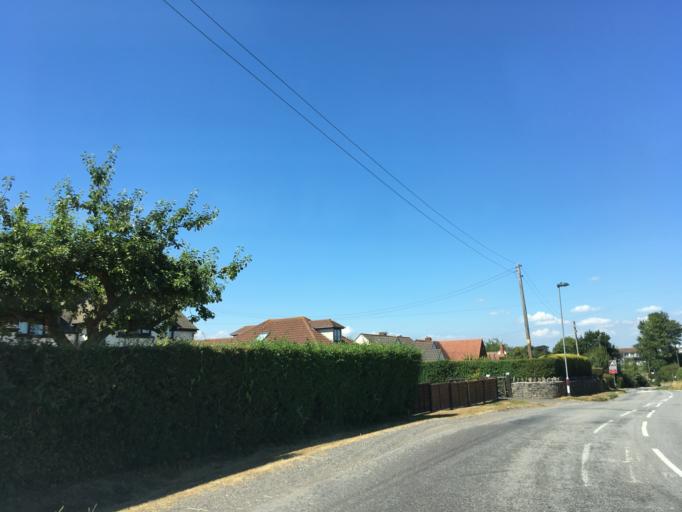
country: GB
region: England
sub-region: South Gloucestershire
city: Chipping Sodbury
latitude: 51.5304
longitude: -2.3973
